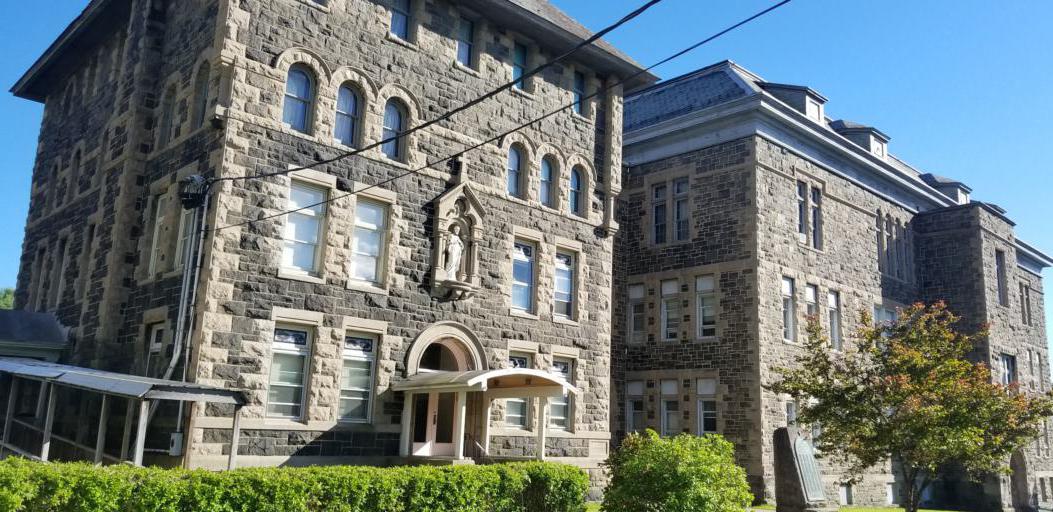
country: US
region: New York
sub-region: Herkimer County
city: Little Falls
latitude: 43.0439
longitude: -74.8534
